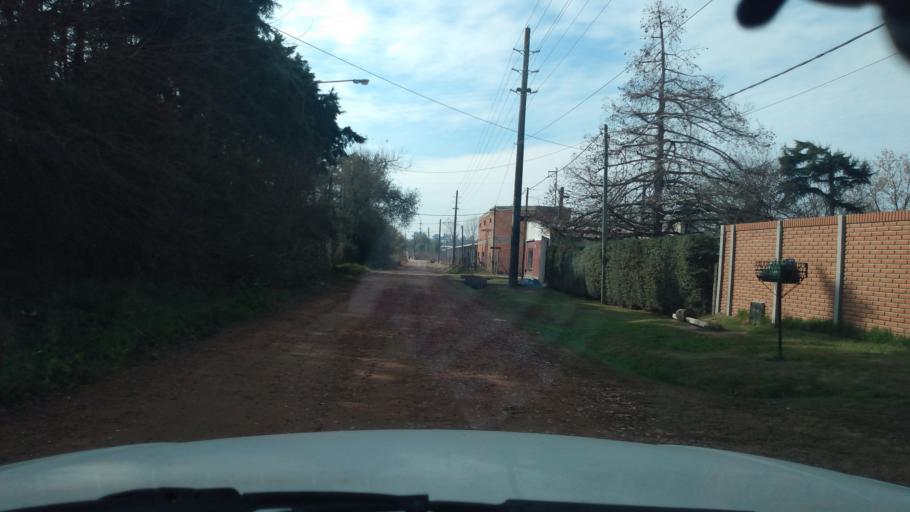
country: AR
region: Buenos Aires
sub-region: Partido de Lujan
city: Lujan
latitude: -34.5873
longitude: -59.1248
